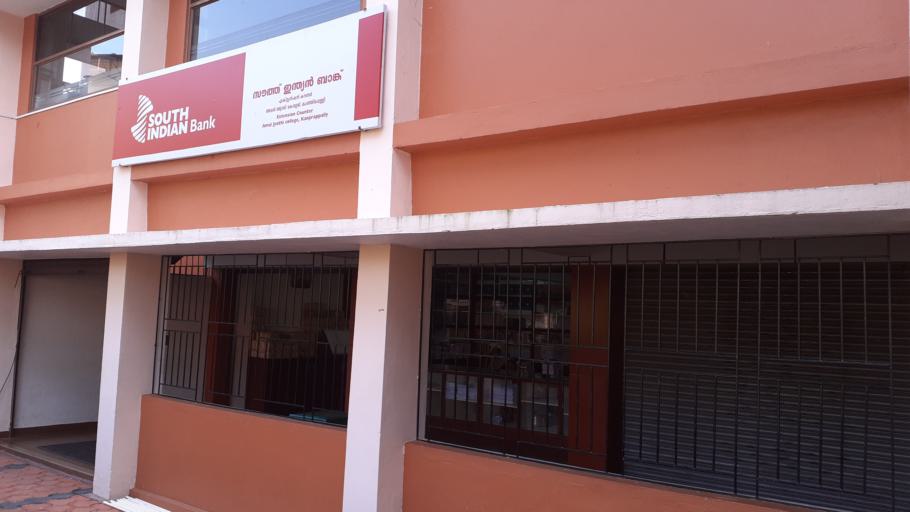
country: IN
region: Kerala
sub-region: Kottayam
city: Erattupetta
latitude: 9.5284
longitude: 76.8213
